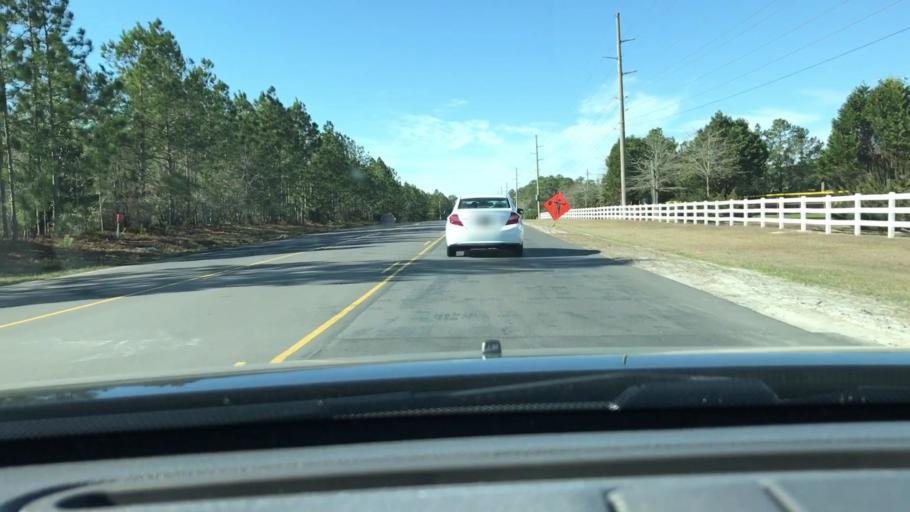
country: US
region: North Carolina
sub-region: Brunswick County
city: Shallotte
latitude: 33.9796
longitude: -78.4118
